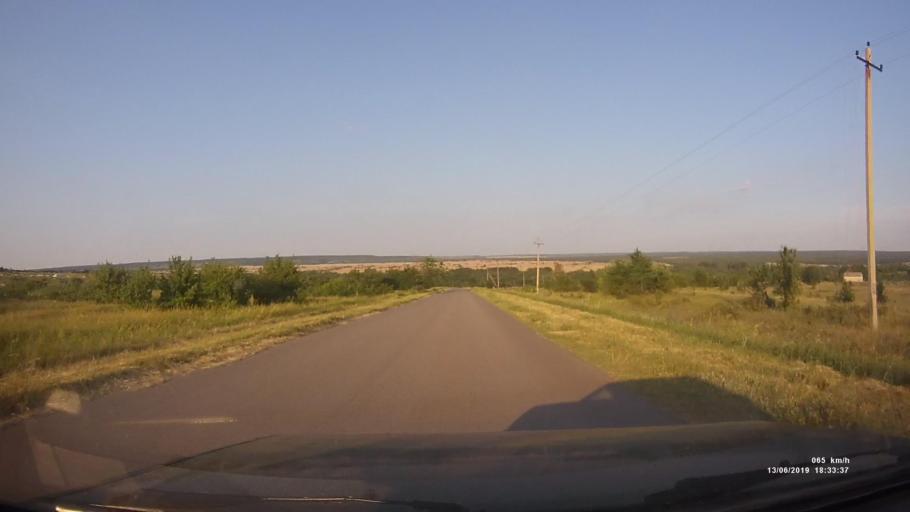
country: RU
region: Rostov
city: Kazanskaya
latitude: 49.8703
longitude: 41.3852
